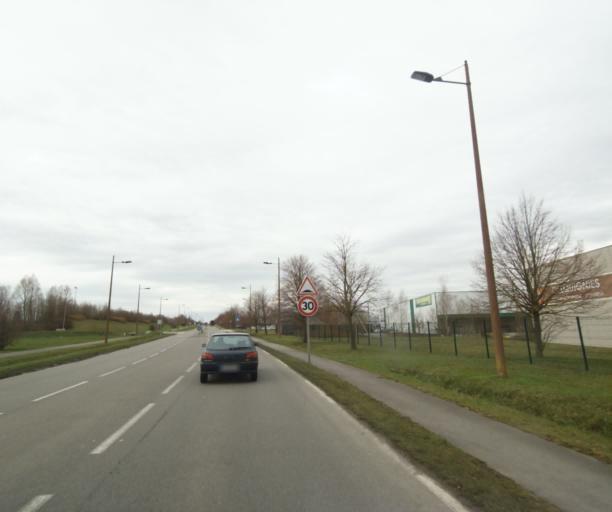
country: FR
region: Nord-Pas-de-Calais
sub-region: Departement du Nord
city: Onnaing
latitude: 50.3723
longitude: 3.6115
